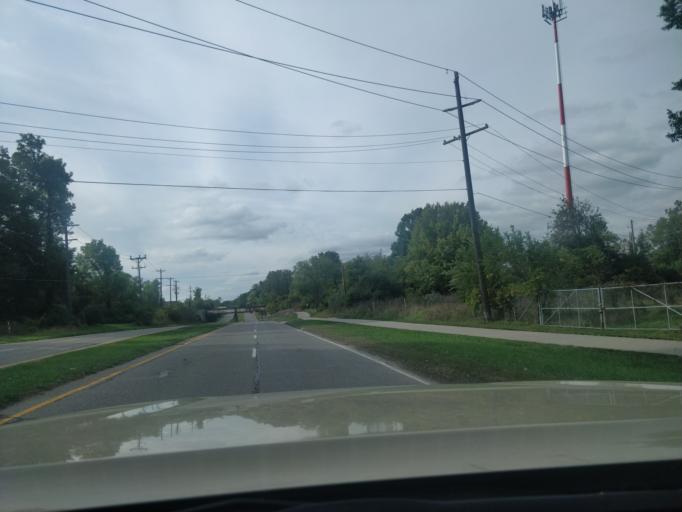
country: US
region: Michigan
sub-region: Wayne County
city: Romulus
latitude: 42.2165
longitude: -83.4157
